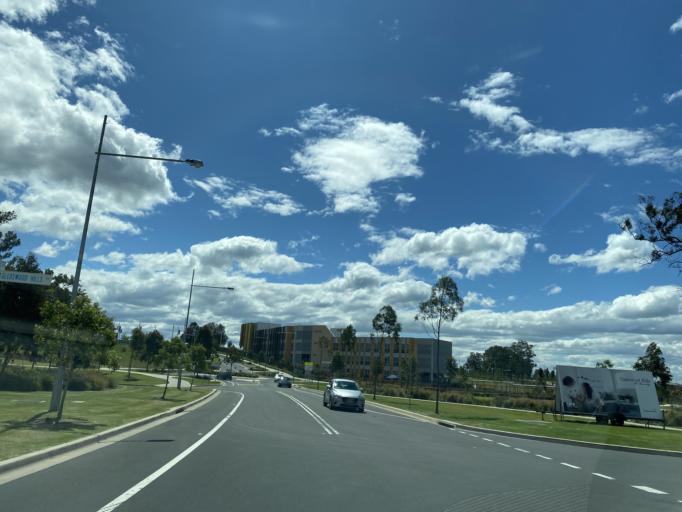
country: AU
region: New South Wales
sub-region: Camden
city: Narellan
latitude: -34.0140
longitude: 150.7770
